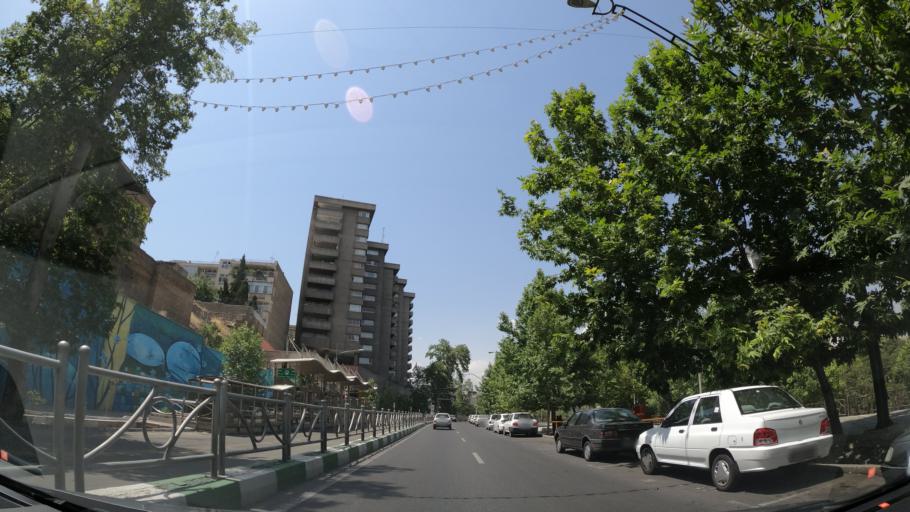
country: IR
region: Tehran
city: Tehran
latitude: 35.7365
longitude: 51.4094
